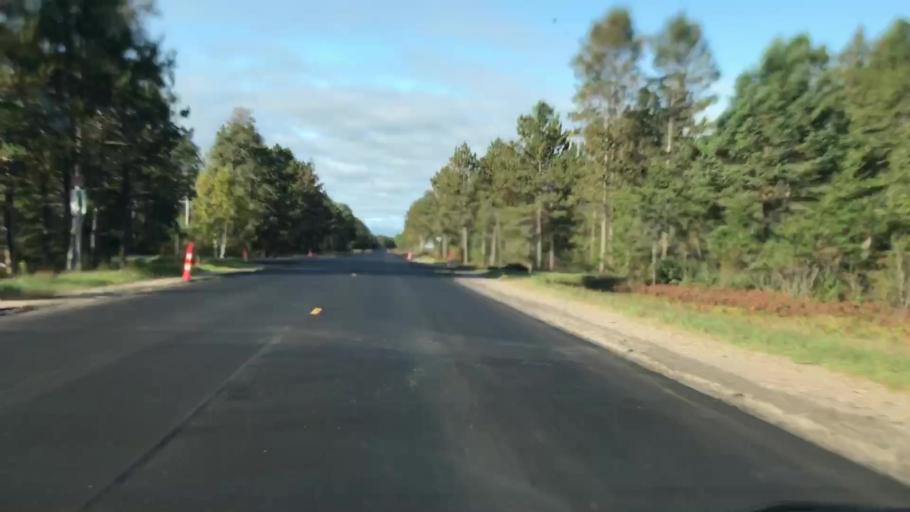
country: US
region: Michigan
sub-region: Mackinac County
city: Saint Ignace
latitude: 46.3519
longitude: -84.9052
